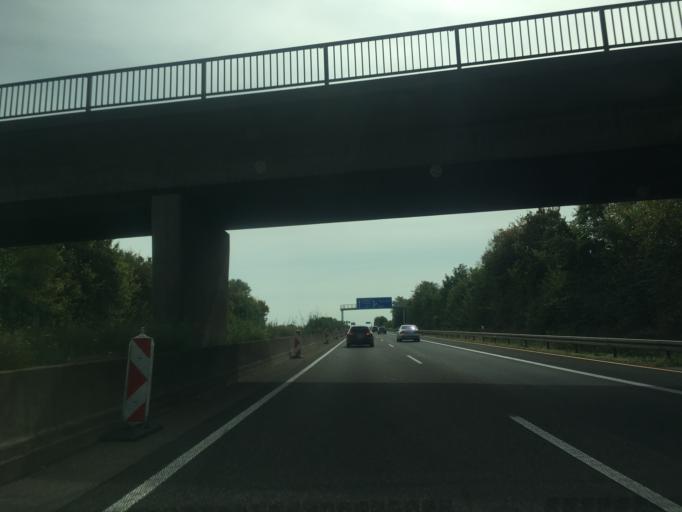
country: DE
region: North Rhine-Westphalia
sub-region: Regierungsbezirk Koln
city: Weilerswist
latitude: 50.7582
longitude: 6.8521
